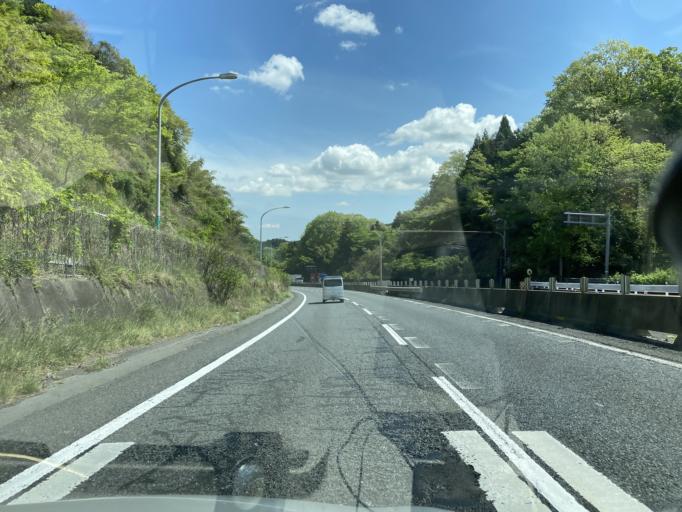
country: JP
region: Mie
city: Nabari
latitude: 34.6561
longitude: 136.0313
